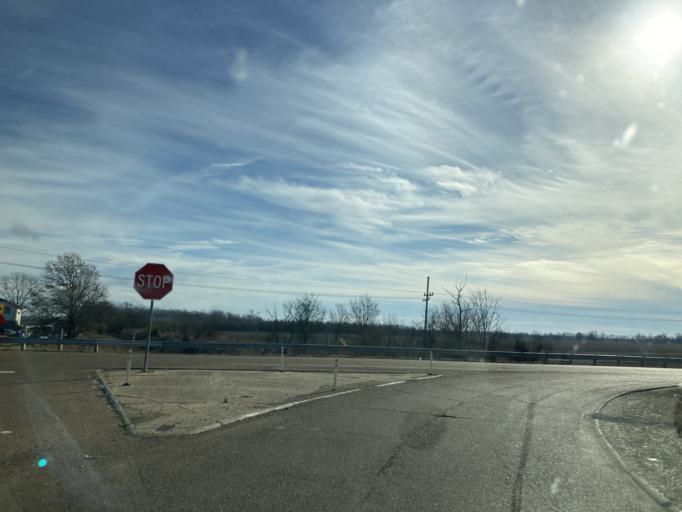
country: US
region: Mississippi
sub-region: Humphreys County
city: Belzoni
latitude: 32.9957
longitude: -90.5884
